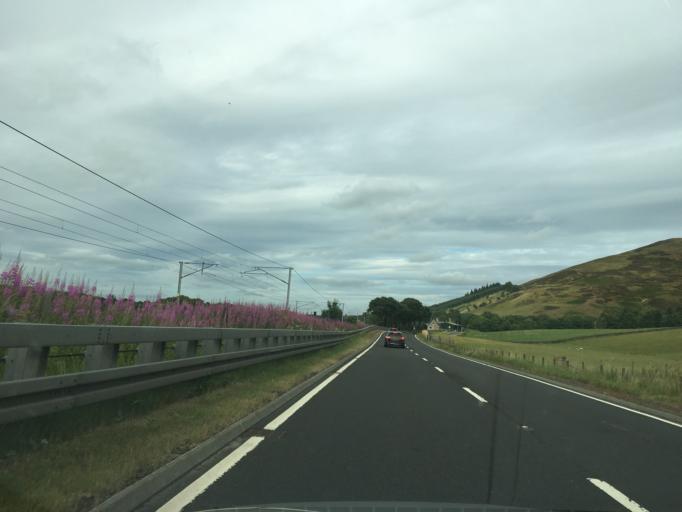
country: GB
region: Scotland
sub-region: South Lanarkshire
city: Biggar
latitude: 55.5469
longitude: -3.6486
